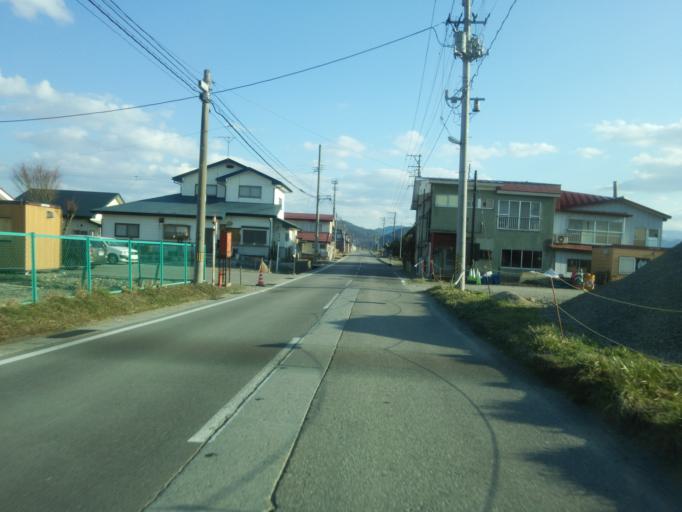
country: JP
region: Fukushima
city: Kitakata
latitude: 37.4738
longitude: 139.8958
